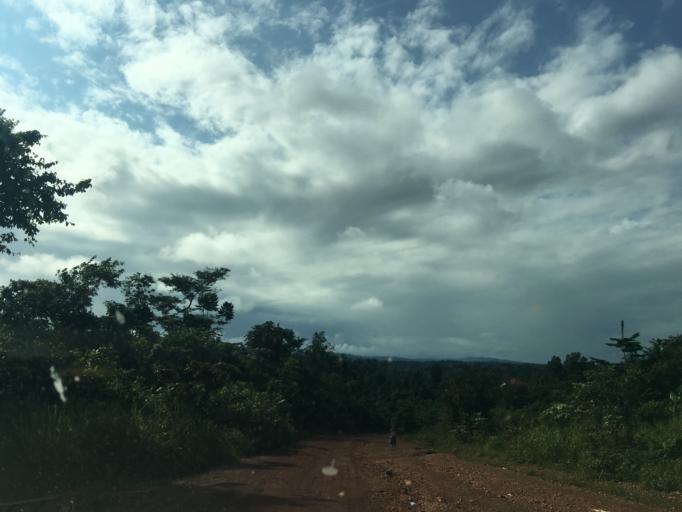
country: GH
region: Western
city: Wassa-Akropong
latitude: 5.9446
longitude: -2.4392
